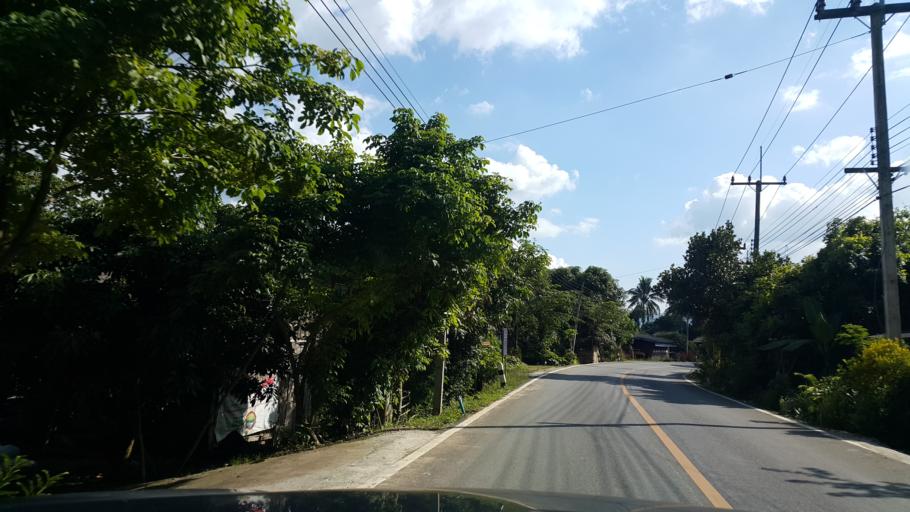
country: TH
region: Lamphun
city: Ban Thi
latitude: 18.5828
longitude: 99.2621
